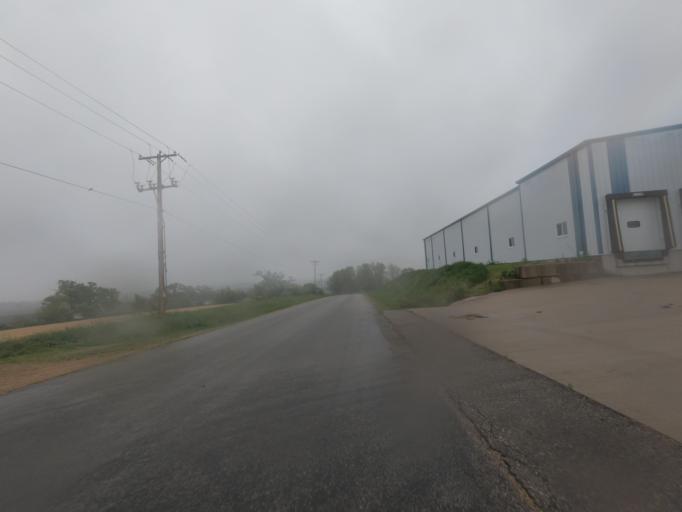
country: US
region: Wisconsin
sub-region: Grant County
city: Hazel Green
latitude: 42.5195
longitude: -90.5358
